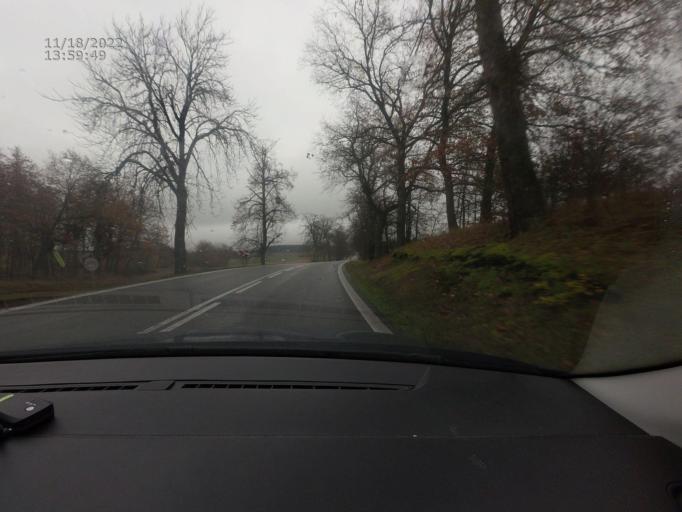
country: CZ
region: Jihocesky
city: Sedlice
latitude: 49.3559
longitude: 14.0060
